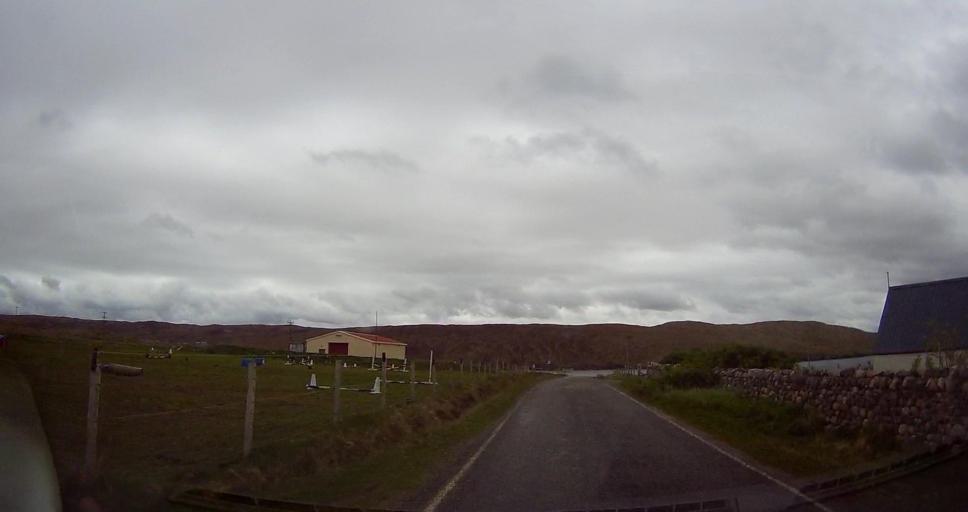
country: GB
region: Scotland
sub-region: Shetland Islands
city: Lerwick
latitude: 60.4845
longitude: -1.4786
